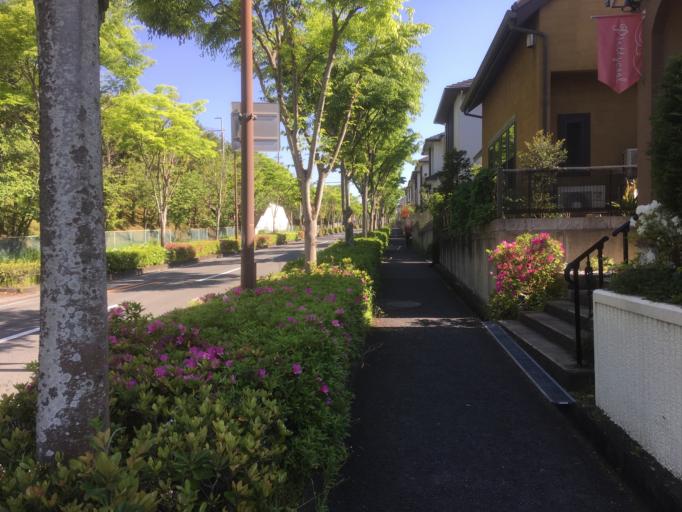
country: JP
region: Nara
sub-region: Ikoma-shi
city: Ikoma
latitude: 34.7256
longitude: 135.7157
